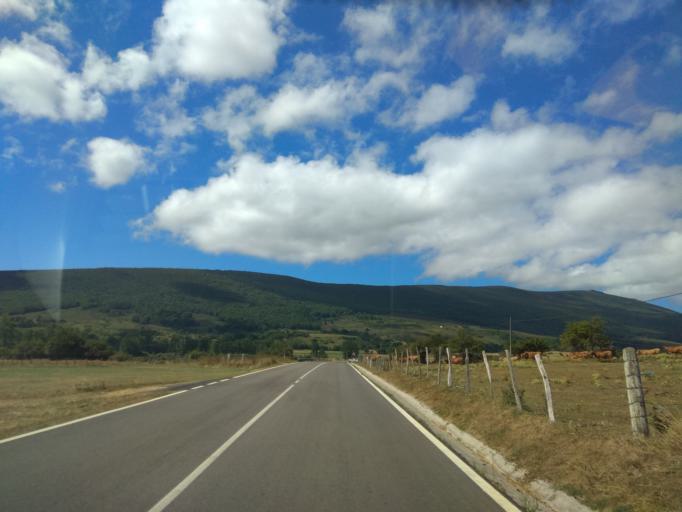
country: ES
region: Cantabria
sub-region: Provincia de Cantabria
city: Villaescusa
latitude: 42.9713
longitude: -4.1601
